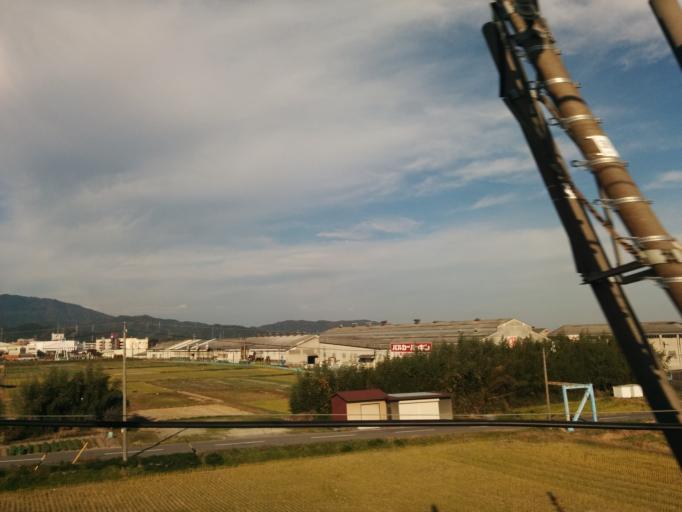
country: JP
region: Gifu
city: Tarui
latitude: 35.3600
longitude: 136.5378
